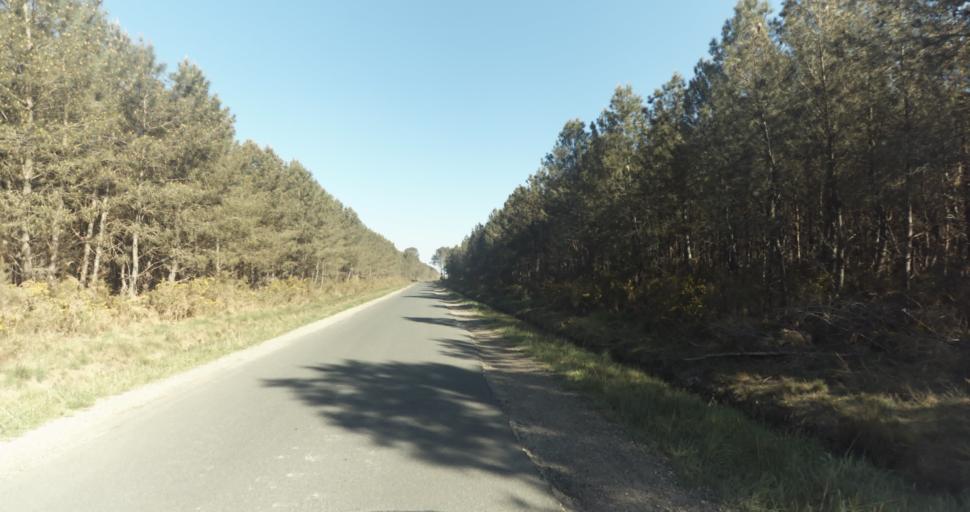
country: FR
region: Aquitaine
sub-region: Departement de la Gironde
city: Marcheprime
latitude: 44.7543
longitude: -0.8496
